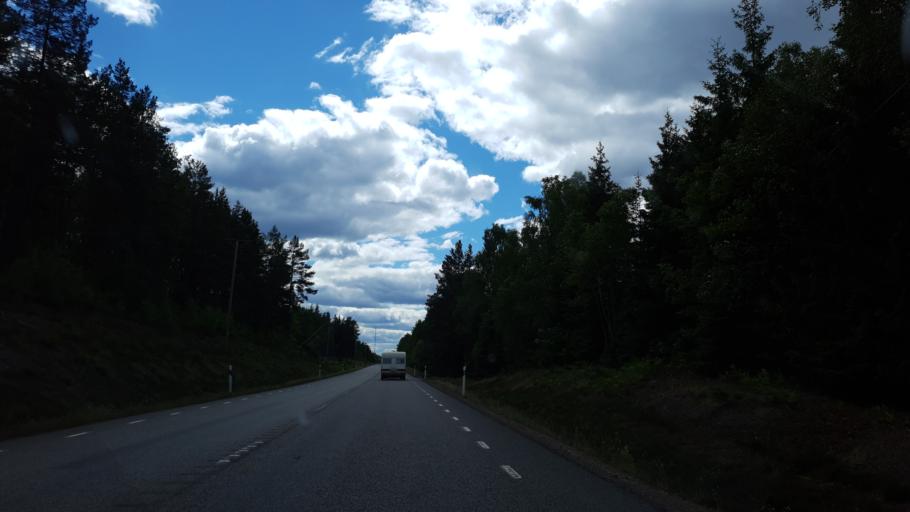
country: SE
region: Kronoberg
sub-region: Vaxjo Kommun
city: Braas
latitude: 57.1461
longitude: 15.1629
